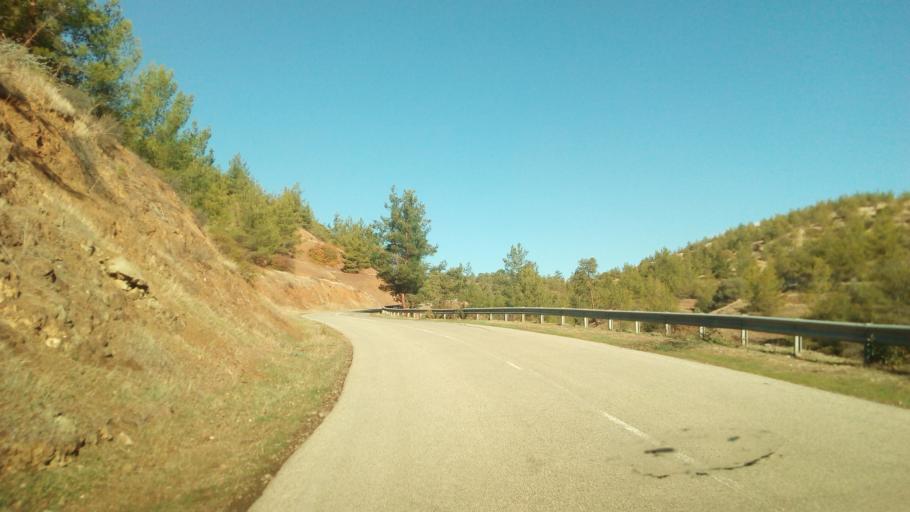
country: CY
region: Lefkosia
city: Lefka
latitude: 35.0845
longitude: 32.8003
